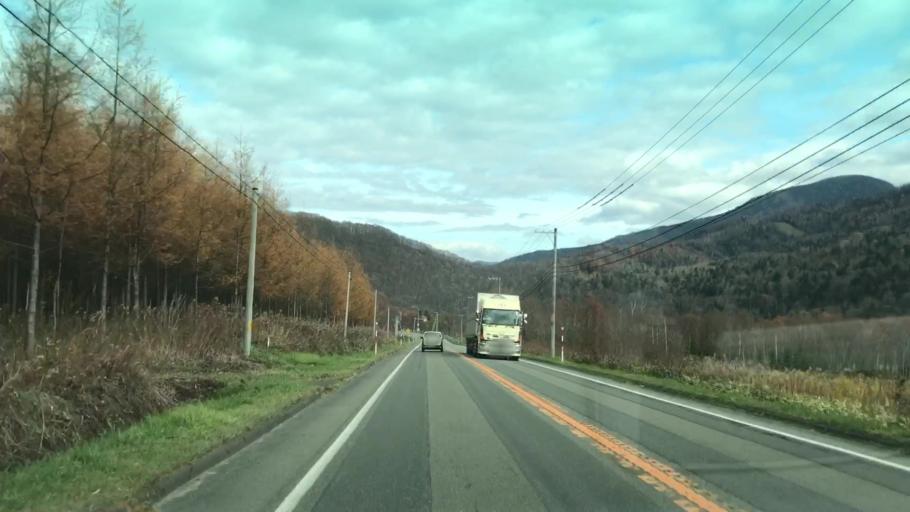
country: JP
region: Hokkaido
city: Shizunai-furukawacho
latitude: 42.7817
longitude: 142.3923
